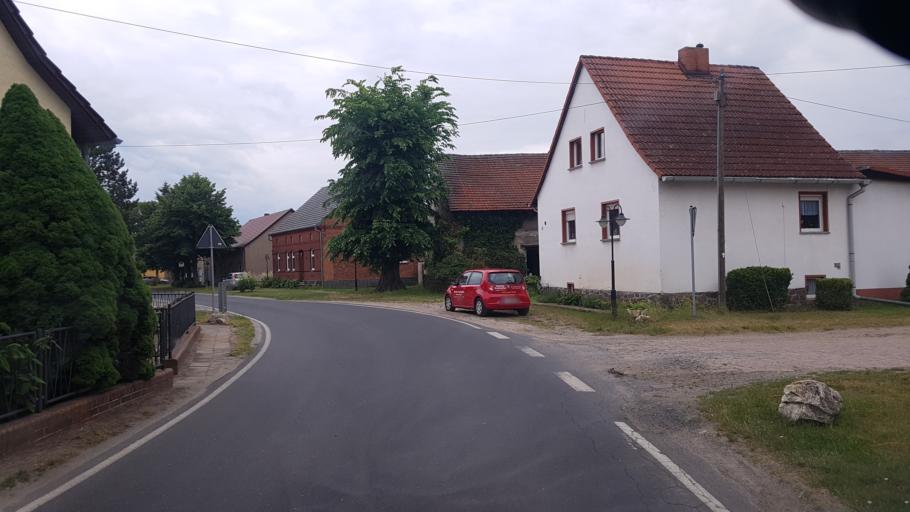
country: DE
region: Saxony-Anhalt
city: Holzdorf
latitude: 51.8002
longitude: 13.2366
